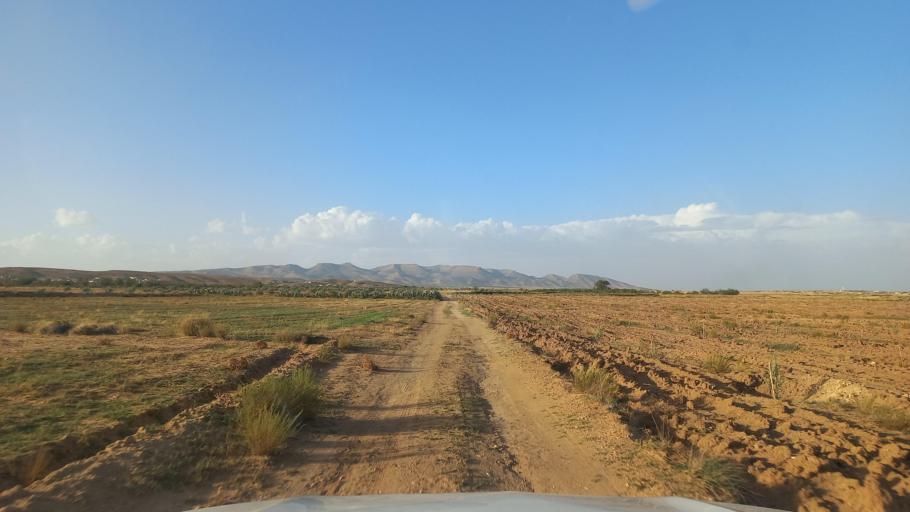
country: TN
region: Al Qasrayn
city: Sbiba
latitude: 35.3626
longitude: 9.0210
